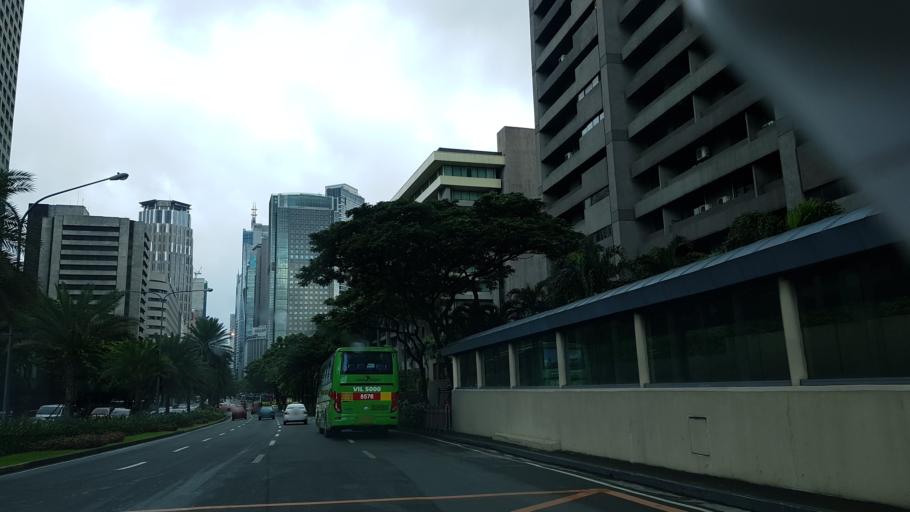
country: PH
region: Metro Manila
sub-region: Makati City
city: Makati City
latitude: 14.5533
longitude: 121.0264
